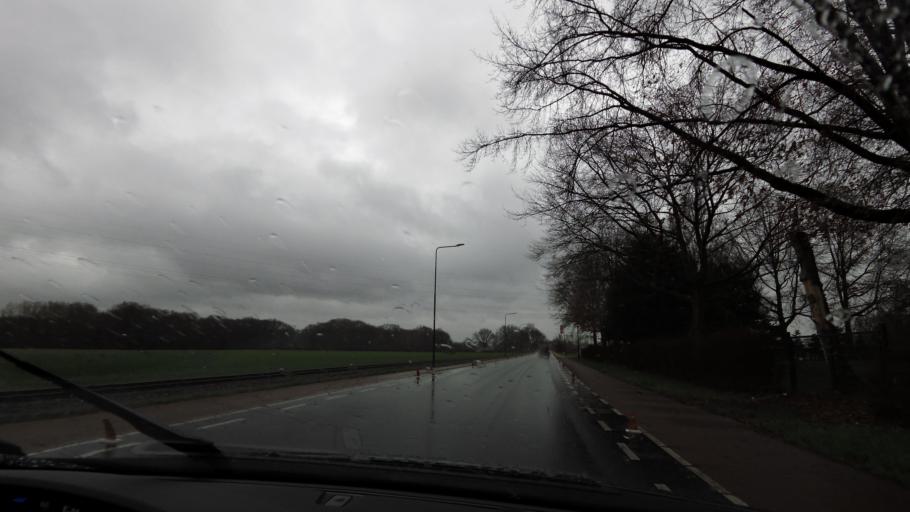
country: NL
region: Limburg
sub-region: Gemeente Sittard-Geleen
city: Born
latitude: 51.0246
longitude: 5.8223
